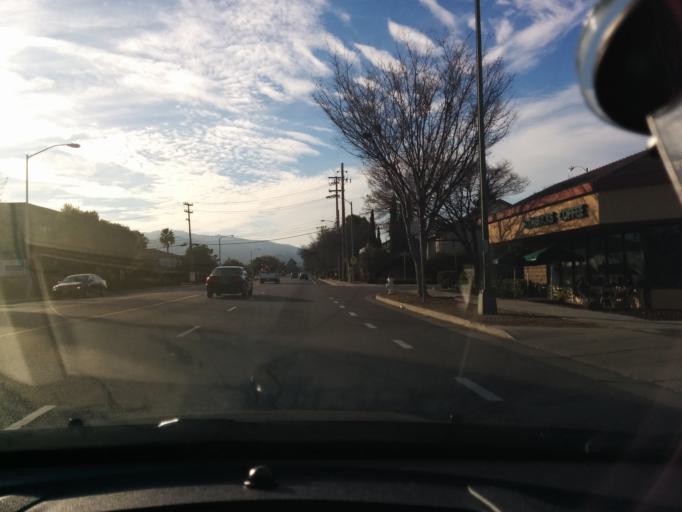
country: US
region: California
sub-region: Santa Clara County
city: Cupertino
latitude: 37.3375
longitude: -122.0426
